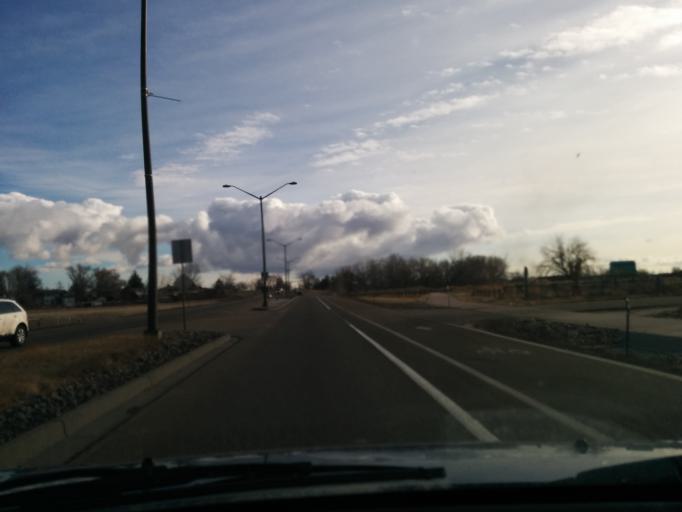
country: US
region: Colorado
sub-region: Larimer County
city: Fort Collins
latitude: 40.5668
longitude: -105.0175
